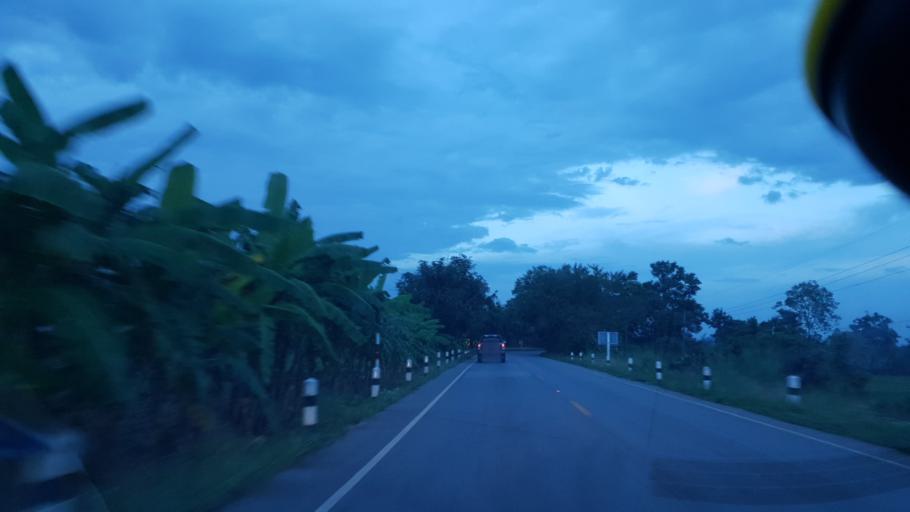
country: TH
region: Chiang Rai
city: Wiang Chiang Rung
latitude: 19.9733
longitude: 99.9742
